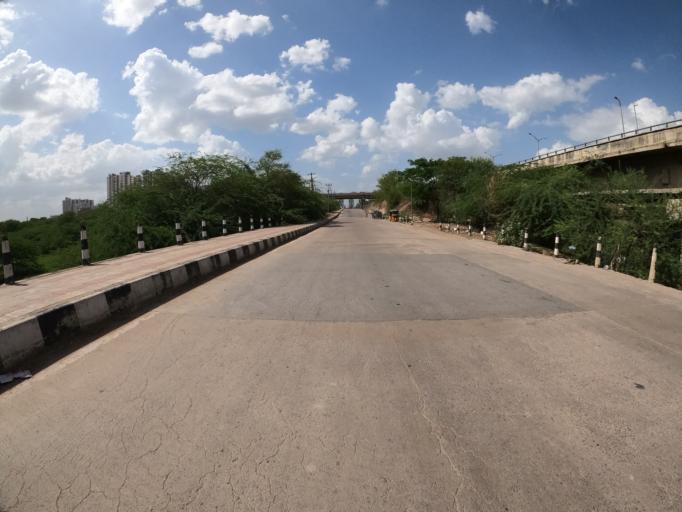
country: IN
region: Telangana
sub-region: Hyderabad
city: Hyderabad
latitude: 17.3843
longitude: 78.3504
